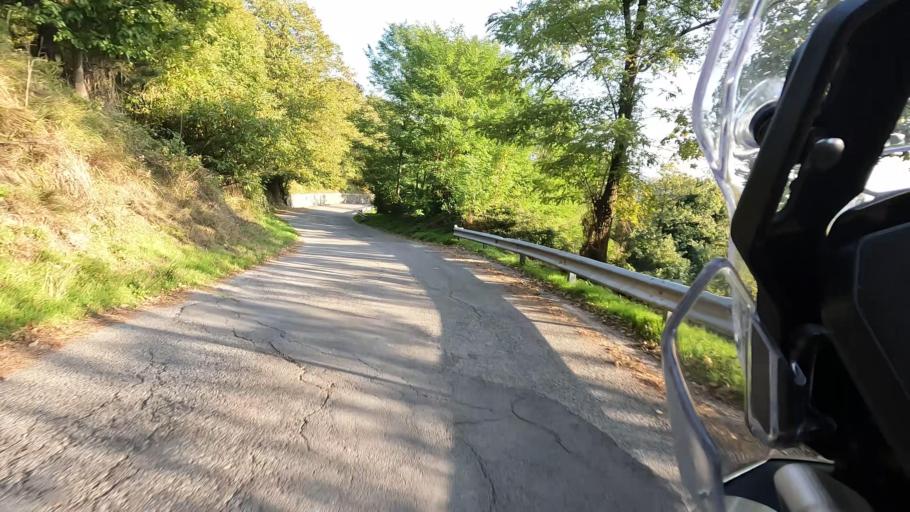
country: IT
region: Liguria
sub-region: Provincia di Savona
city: San Giovanni
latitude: 44.4108
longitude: 8.5190
